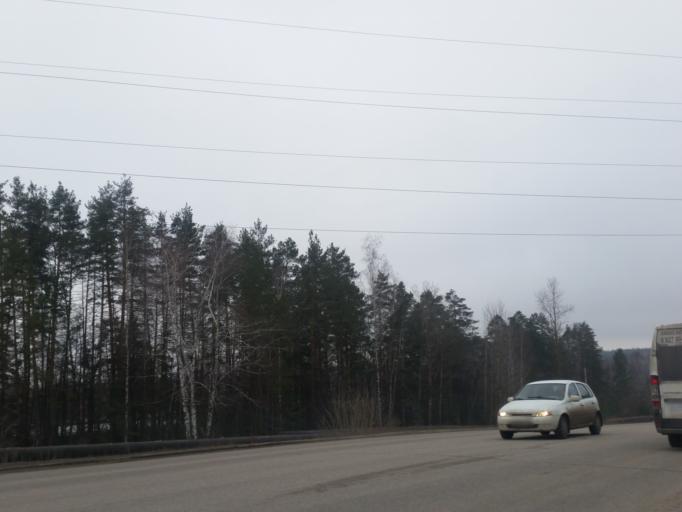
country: RU
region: Ulyanovsk
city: Dimitrovgrad
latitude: 54.2158
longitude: 49.5477
